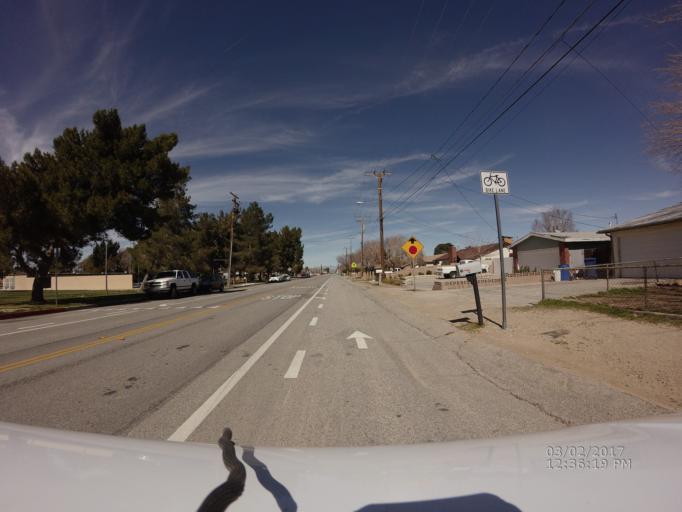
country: US
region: California
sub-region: Los Angeles County
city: Quartz Hill
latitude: 34.6512
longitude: -118.2273
